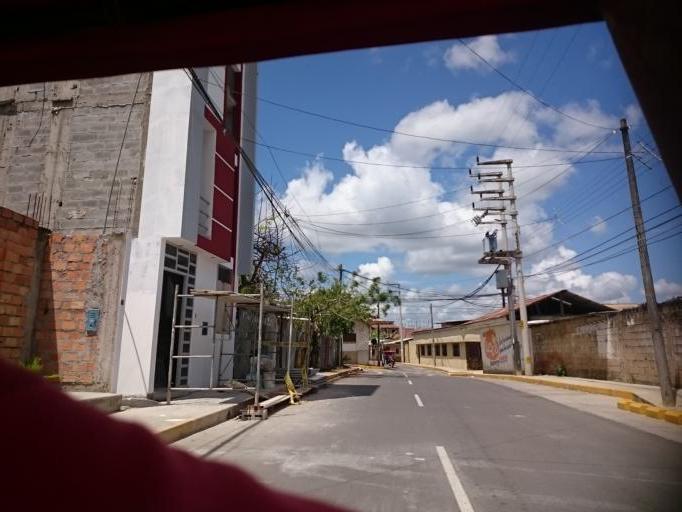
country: PE
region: San Martin
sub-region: Provincia de San Martin
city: Tarapoto
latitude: -6.4843
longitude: -76.3570
